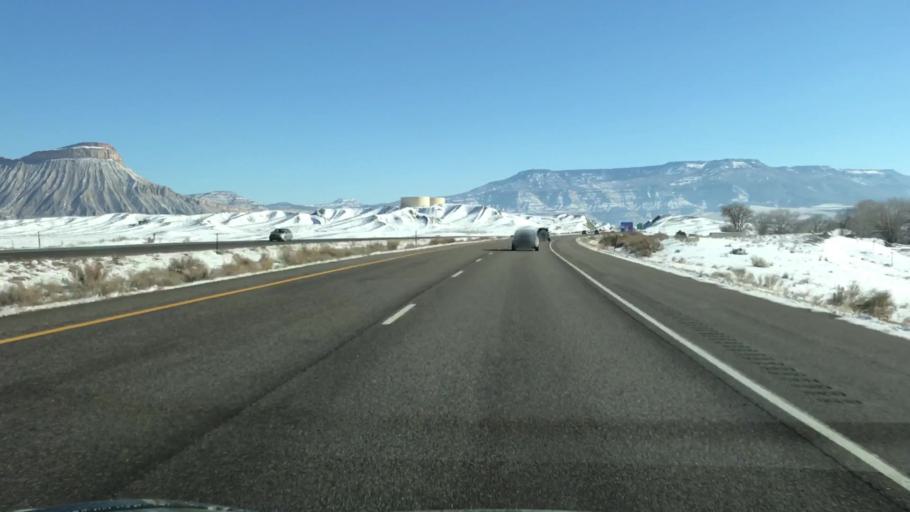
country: US
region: Colorado
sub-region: Mesa County
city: Clifton
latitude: 39.1048
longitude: -108.4733
